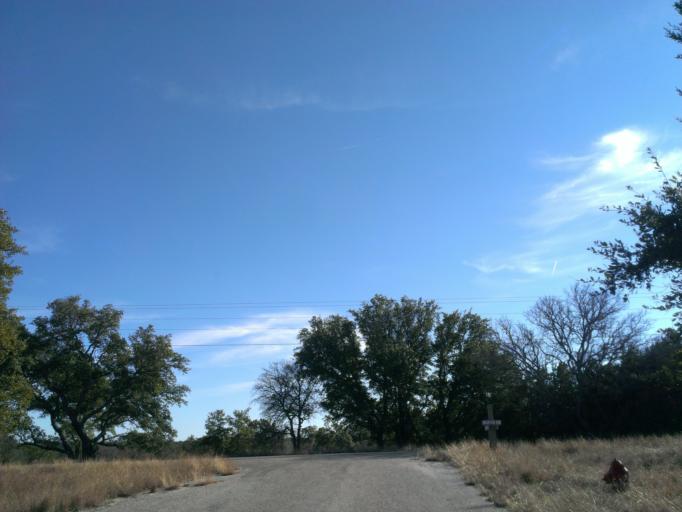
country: US
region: Texas
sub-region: Llano County
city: Horseshoe Bay
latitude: 30.5344
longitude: -98.3364
